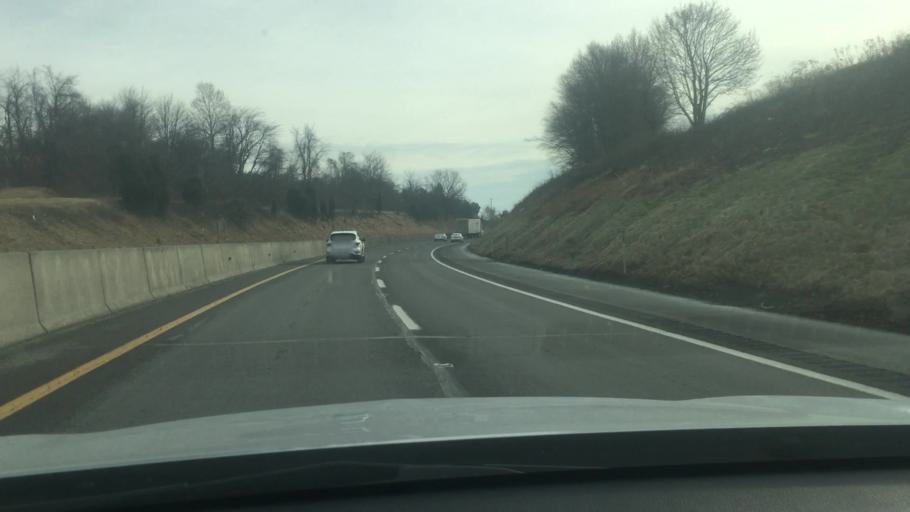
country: US
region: Pennsylvania
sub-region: Chester County
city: Elverson
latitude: 40.1502
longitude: -75.8407
